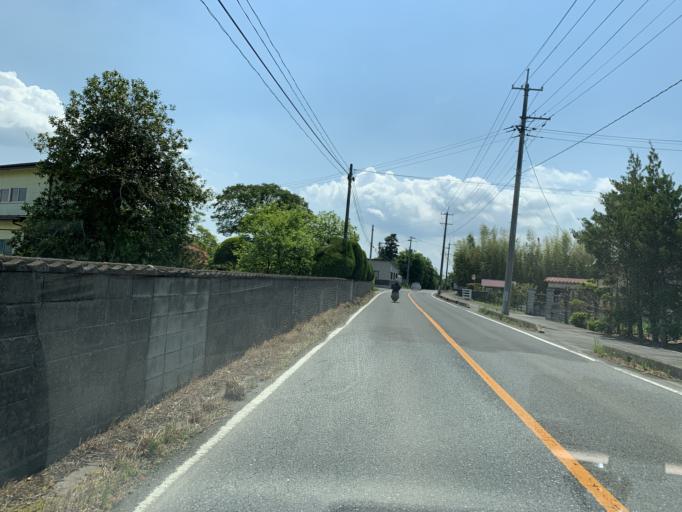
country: JP
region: Miyagi
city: Kogota
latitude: 38.5741
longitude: 141.0363
